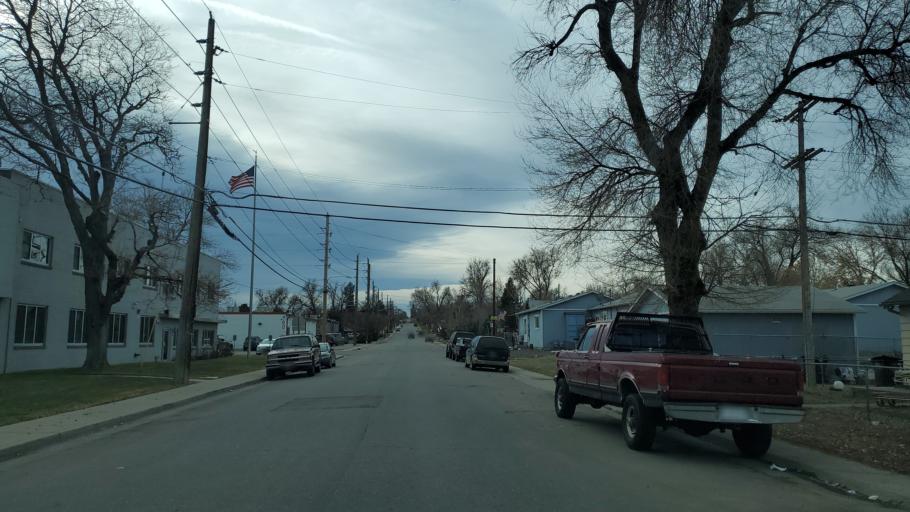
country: US
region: Colorado
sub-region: Denver County
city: Denver
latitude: 39.7092
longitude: -105.0039
